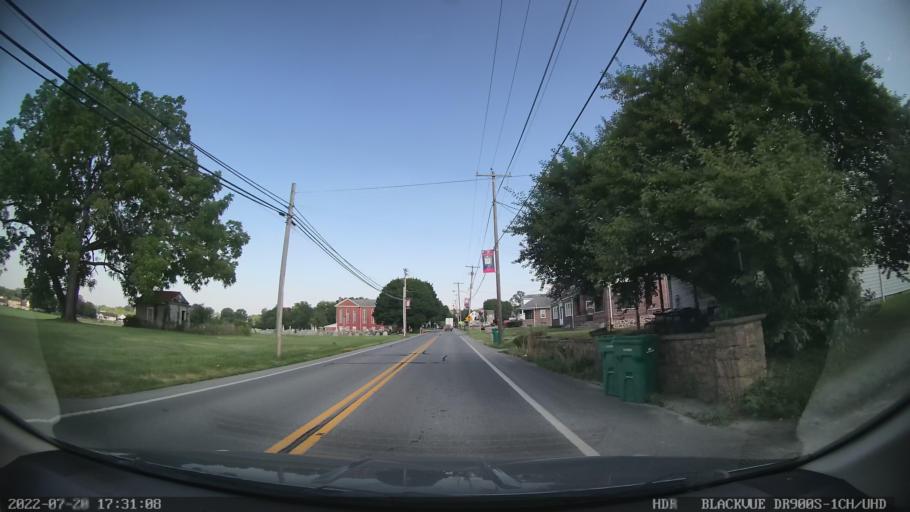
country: US
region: Pennsylvania
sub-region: Berks County
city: Blandon
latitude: 40.4427
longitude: -75.8892
